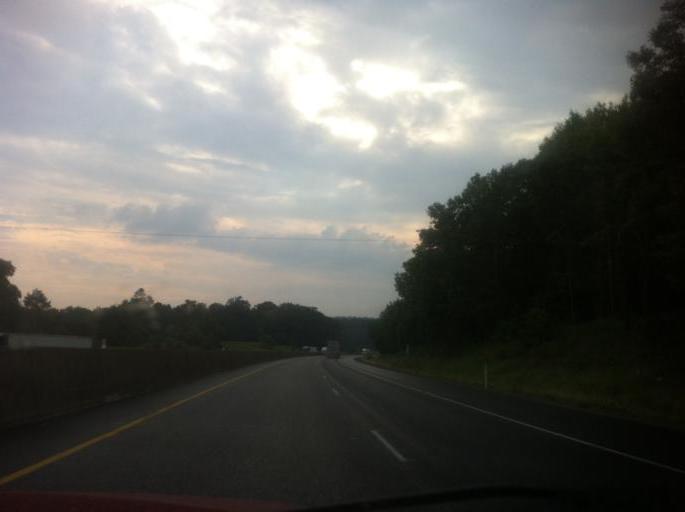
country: US
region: Pennsylvania
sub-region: Clarion County
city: Marianne
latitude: 41.1959
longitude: -79.4531
